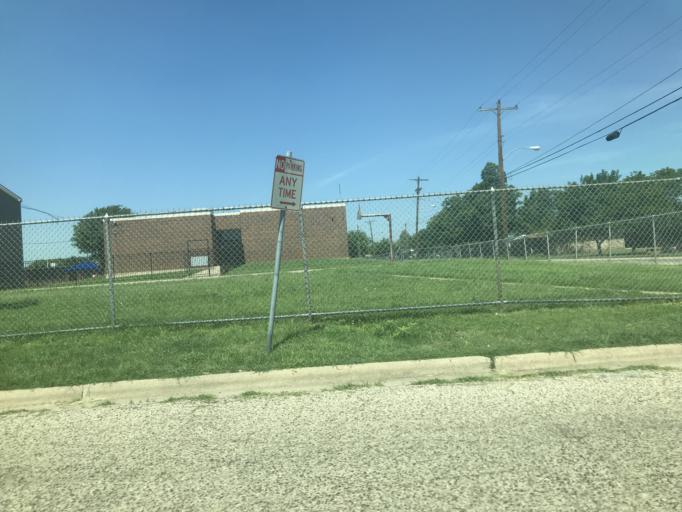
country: US
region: Texas
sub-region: Taylor County
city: Abilene
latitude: 32.4698
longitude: -99.7361
